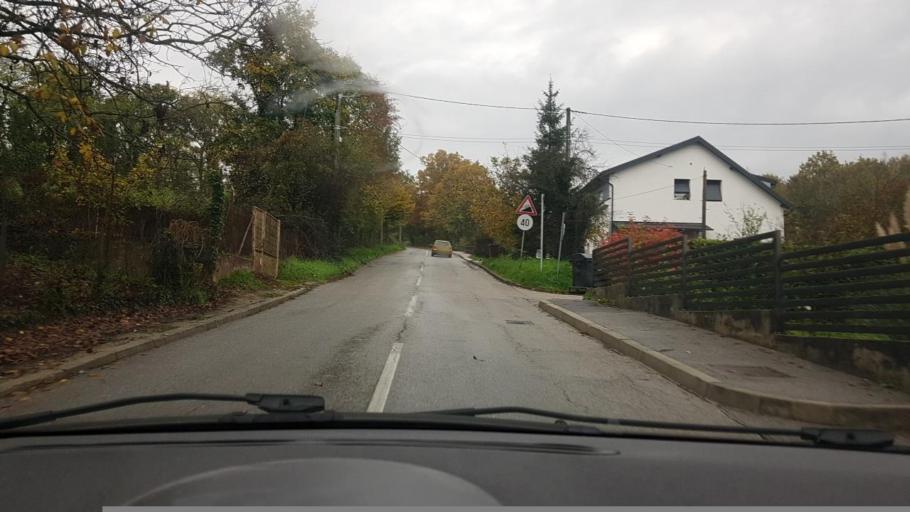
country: HR
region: Grad Zagreb
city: Zagreb
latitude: 45.8372
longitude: 15.9995
